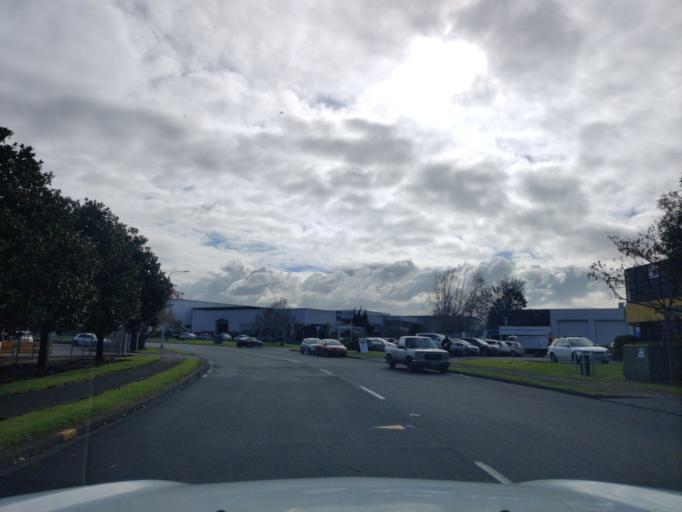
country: NZ
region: Auckland
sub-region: Auckland
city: Manukau City
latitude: -36.9420
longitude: 174.8818
